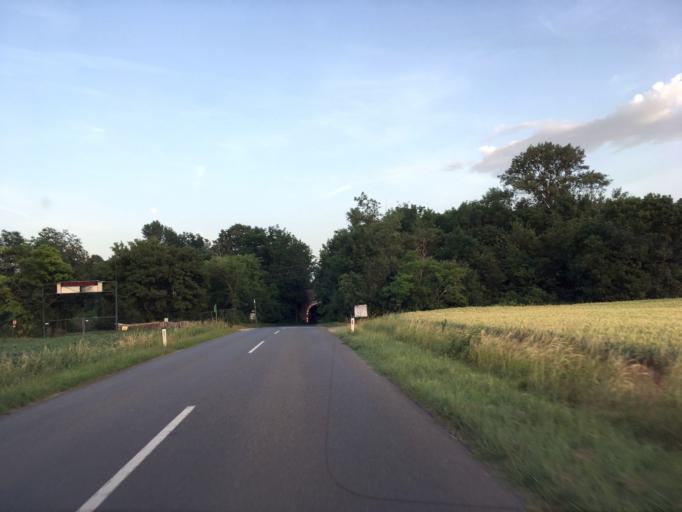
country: AT
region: Lower Austria
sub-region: Politischer Bezirk Baden
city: Teesdorf
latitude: 47.9541
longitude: 16.2779
